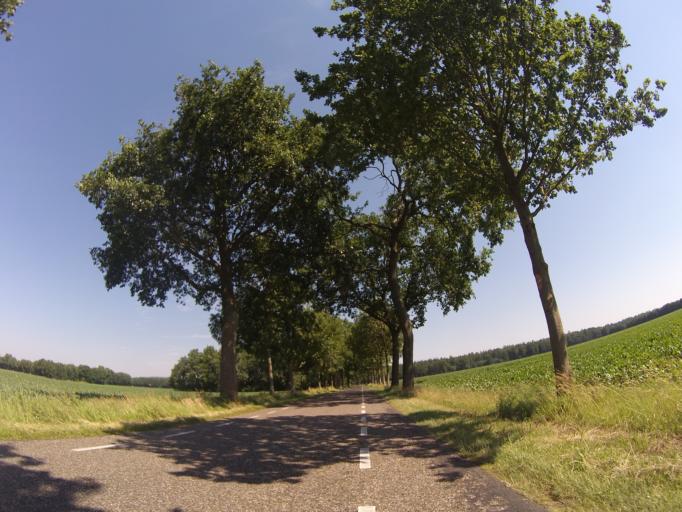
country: NL
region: Drenthe
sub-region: Gemeente Coevorden
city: Sleen
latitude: 52.8157
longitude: 6.7419
